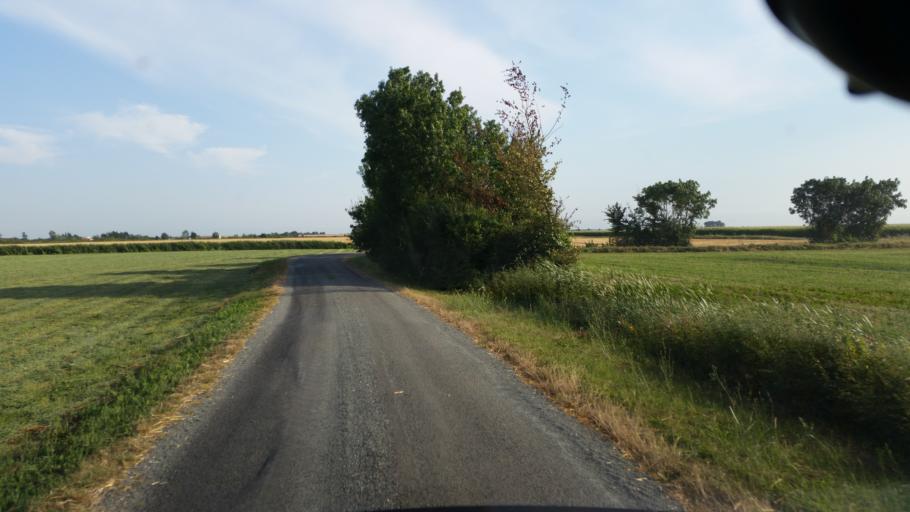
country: FR
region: Poitou-Charentes
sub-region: Departement de la Charente-Maritime
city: Marans
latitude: 46.3116
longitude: -0.9470
